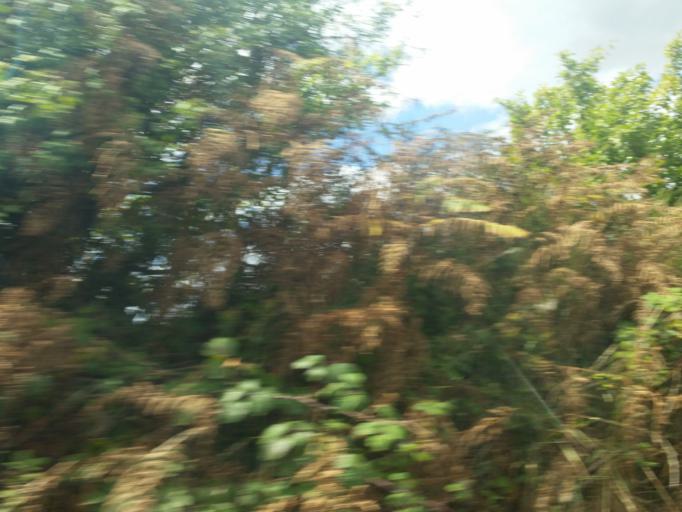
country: IE
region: Munster
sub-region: Waterford
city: Portlaw
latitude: 52.1803
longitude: -7.3840
